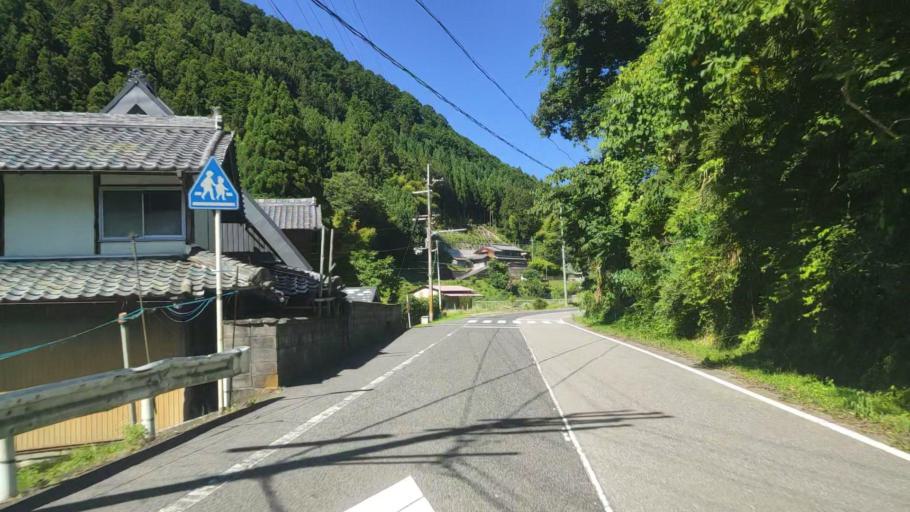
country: JP
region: Nara
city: Yoshino-cho
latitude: 34.4109
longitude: 135.9313
